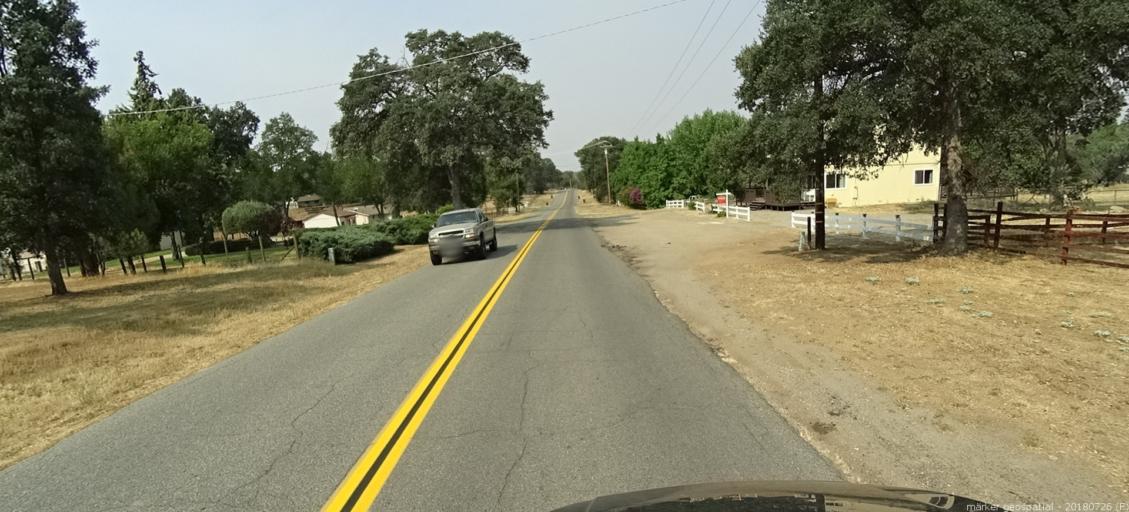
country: US
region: California
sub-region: Madera County
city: Coarsegold
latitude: 37.2151
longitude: -119.6828
